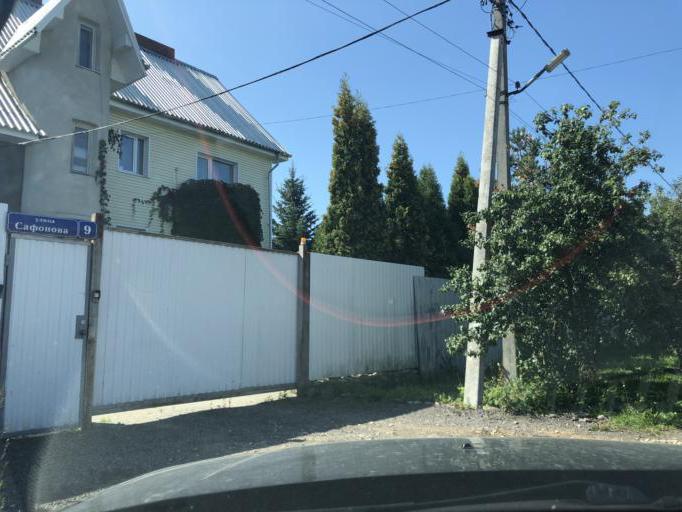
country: RU
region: Tula
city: Mendeleyevskiy
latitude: 54.1802
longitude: 37.5484
